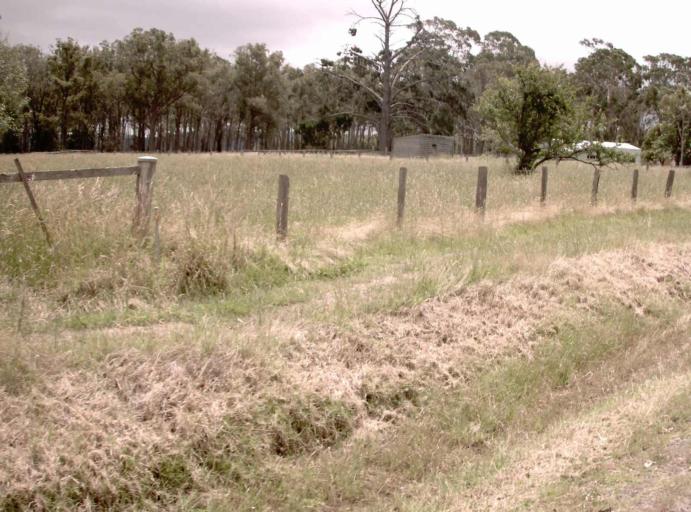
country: AU
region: Victoria
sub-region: Latrobe
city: Traralgon
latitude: -38.5419
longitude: 146.6564
